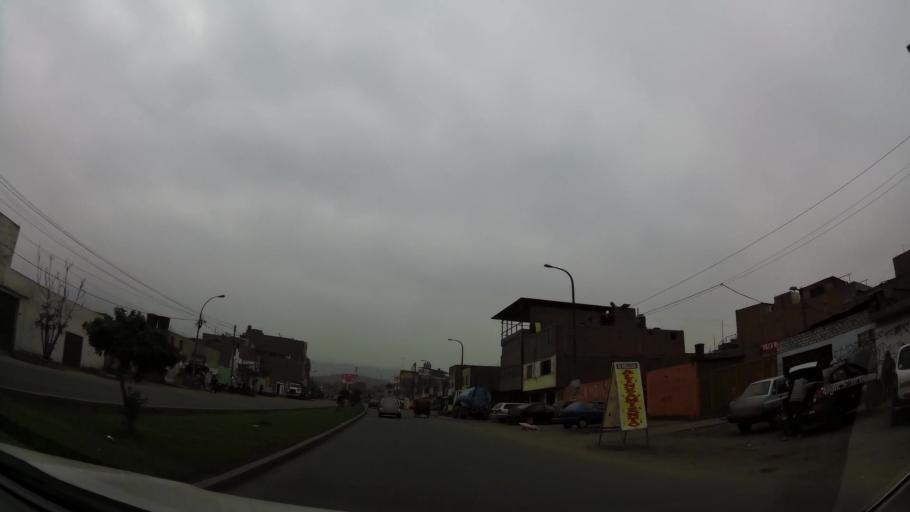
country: PE
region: Lima
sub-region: Lima
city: Independencia
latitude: -11.9727
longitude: -76.9917
